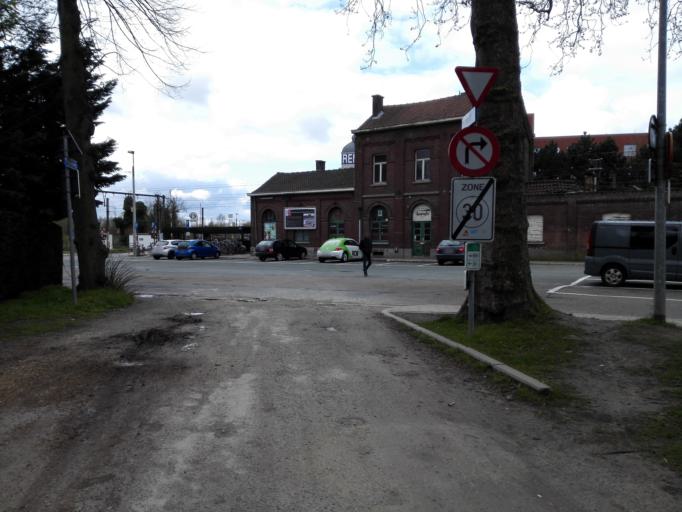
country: BE
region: Flanders
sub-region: Provincie Vlaams-Brabant
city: Rotselaar
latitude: 50.9230
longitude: 4.7020
